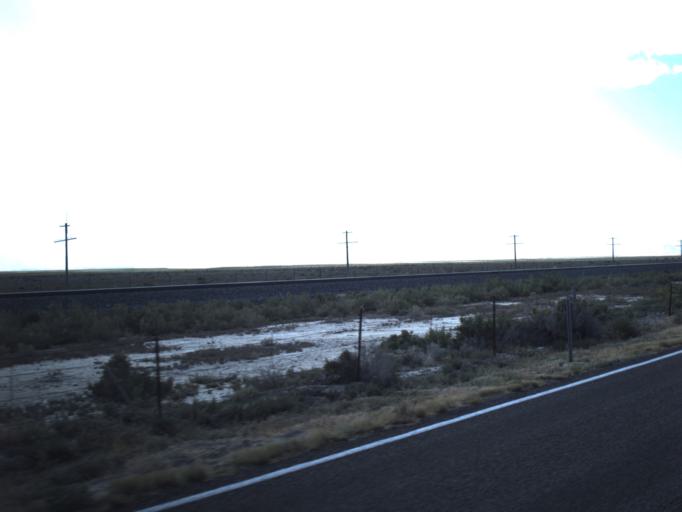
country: US
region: Utah
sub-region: Millard County
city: Delta
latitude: 39.0374
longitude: -112.7727
